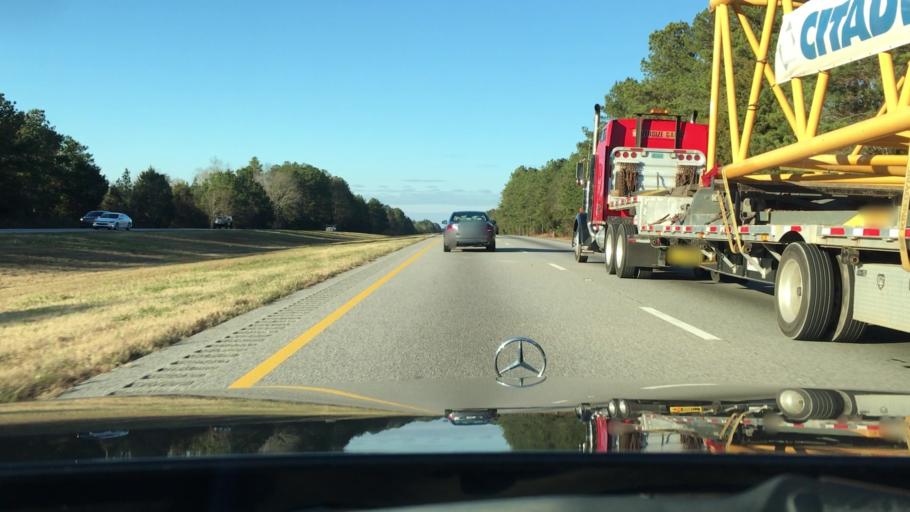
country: US
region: South Carolina
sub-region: Chester County
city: Great Falls
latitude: 34.6799
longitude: -81.0292
